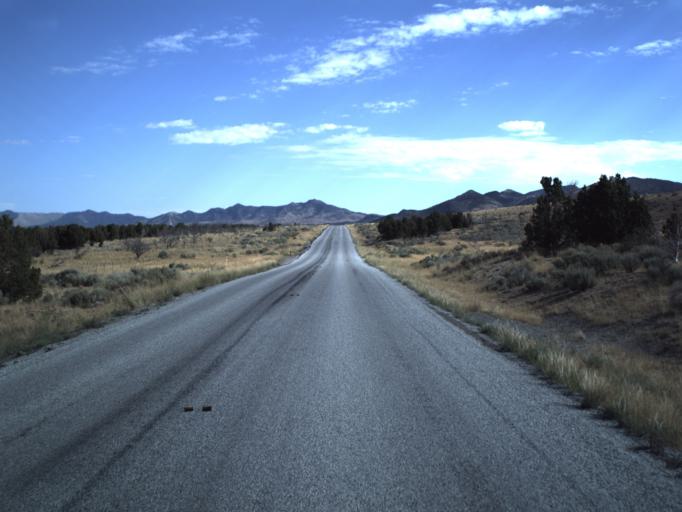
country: US
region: Utah
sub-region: Juab County
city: Mona
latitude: 39.7859
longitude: -112.1504
